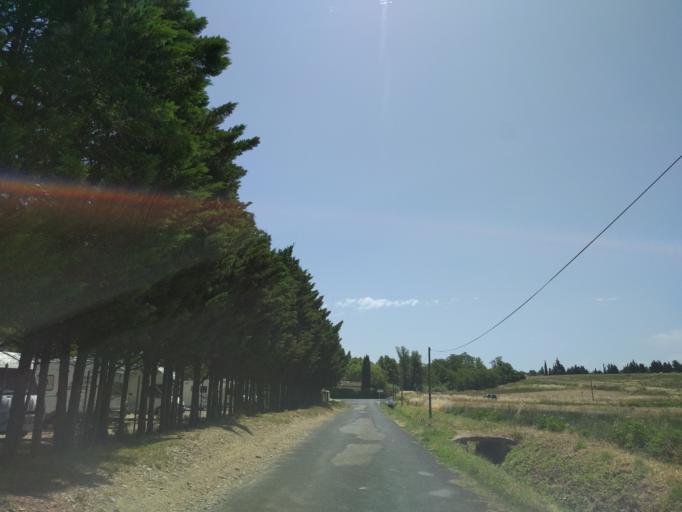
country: FR
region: Languedoc-Roussillon
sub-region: Departement de l'Aude
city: Carcassonne
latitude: 43.2004
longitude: 2.3519
